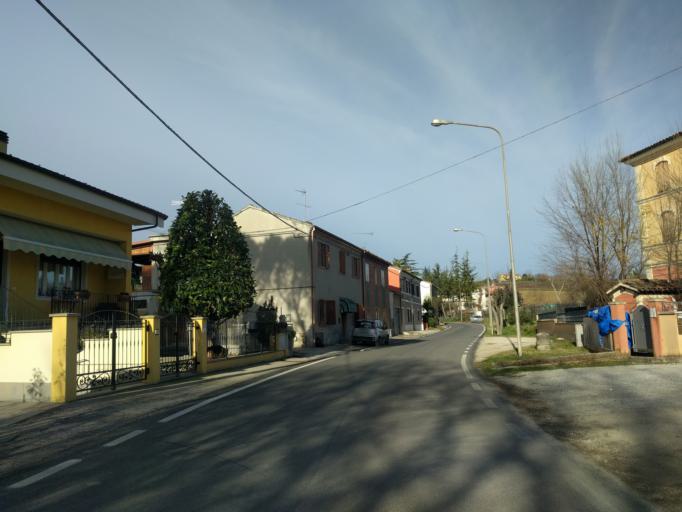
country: IT
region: The Marches
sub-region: Provincia di Pesaro e Urbino
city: Cuccurano
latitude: 43.7946
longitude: 12.9532
